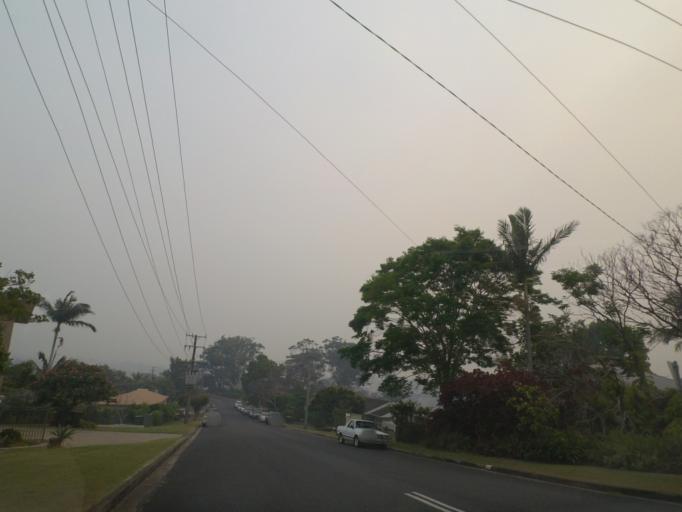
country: AU
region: New South Wales
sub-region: Coffs Harbour
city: Coffs Harbour
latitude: -30.3033
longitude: 153.1126
